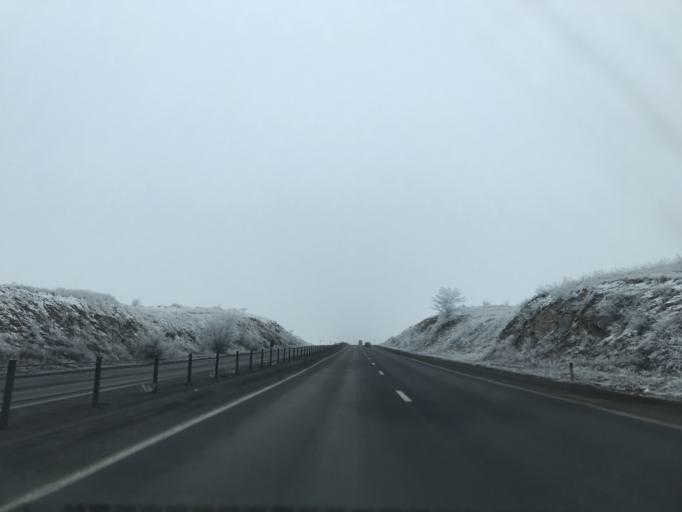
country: RU
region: Rostov
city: Likhoy
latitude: 48.1455
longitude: 40.2601
